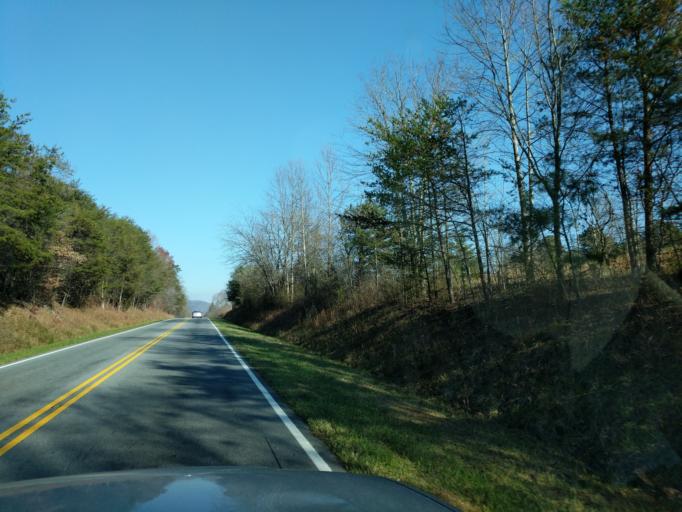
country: US
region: North Carolina
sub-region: McDowell County
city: West Marion
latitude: 35.5985
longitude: -81.9840
